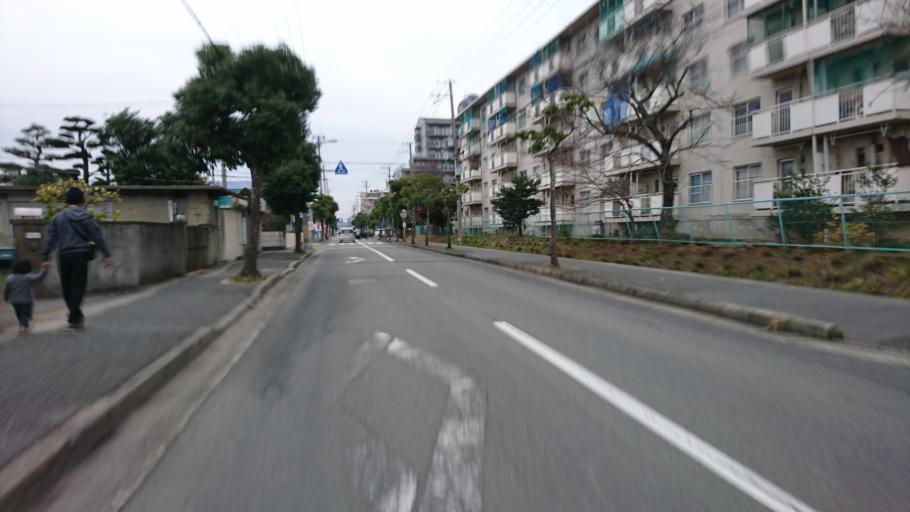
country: JP
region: Hyogo
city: Kakogawacho-honmachi
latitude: 34.7669
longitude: 134.8219
